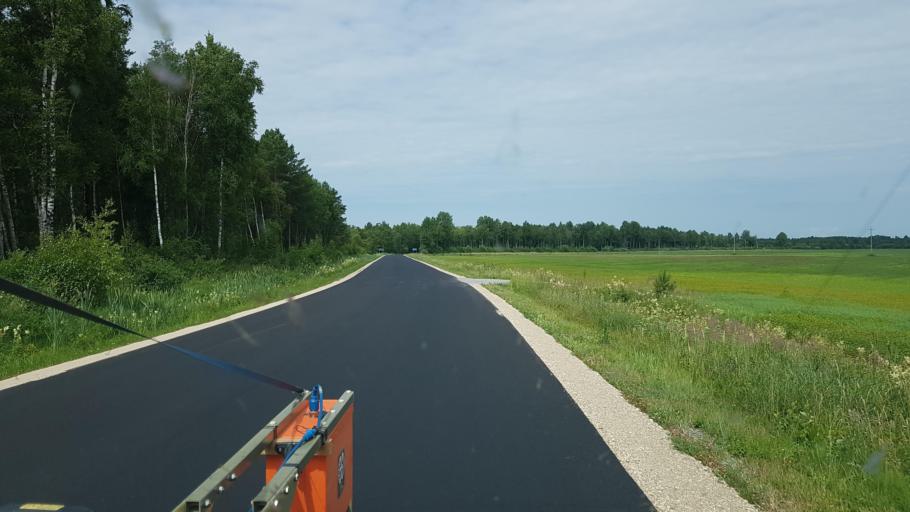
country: EE
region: Paernumaa
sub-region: Halinga vald
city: Parnu-Jaagupi
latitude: 58.6214
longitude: 24.2712
